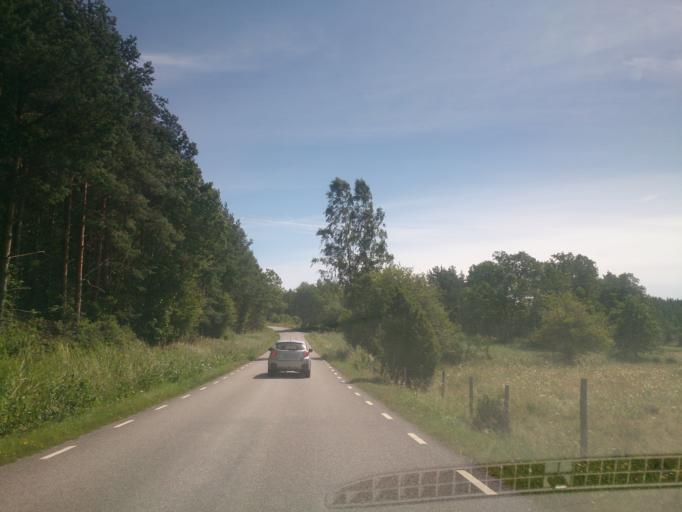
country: SE
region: OEstergoetland
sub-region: Valdemarsviks Kommun
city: Valdemarsvik
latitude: 58.2720
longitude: 16.7305
